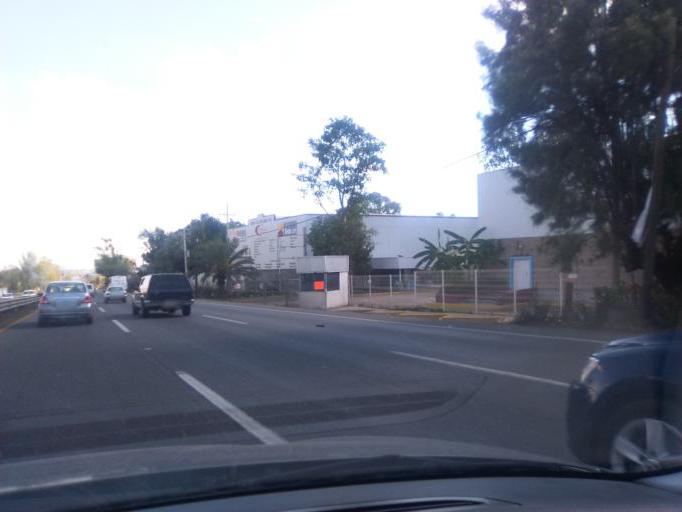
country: MX
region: Guanajuato
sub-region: Silao de la Victoria
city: El Refugio de los Sauces
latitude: 21.0357
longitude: -101.5530
